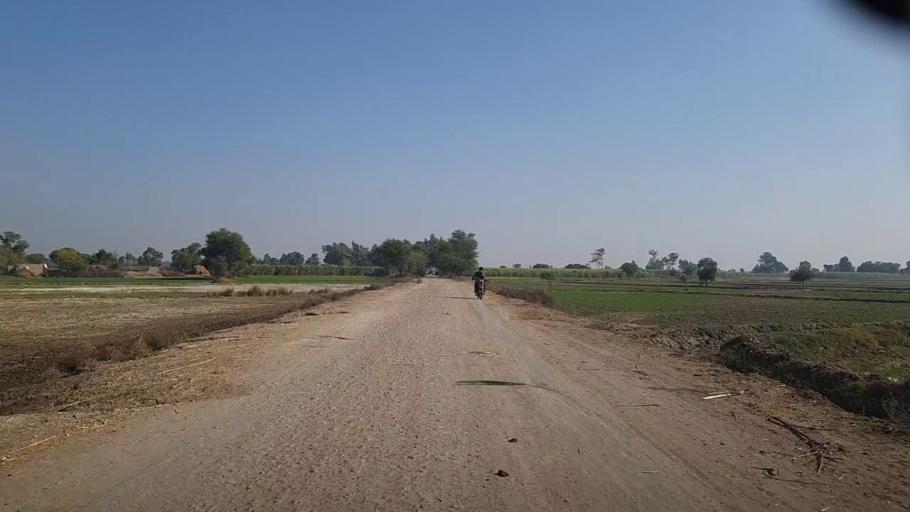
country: PK
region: Sindh
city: Darya Khan Marri
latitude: 26.6543
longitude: 68.3564
